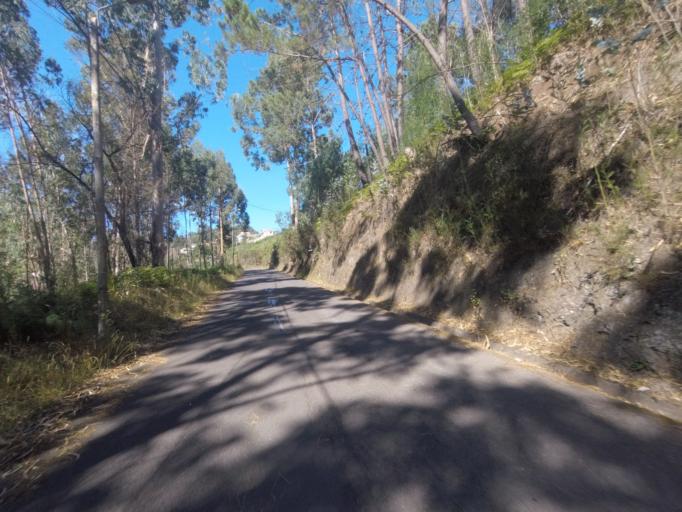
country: PT
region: Madeira
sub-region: Ribeira Brava
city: Campanario
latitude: 32.6919
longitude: -17.0195
